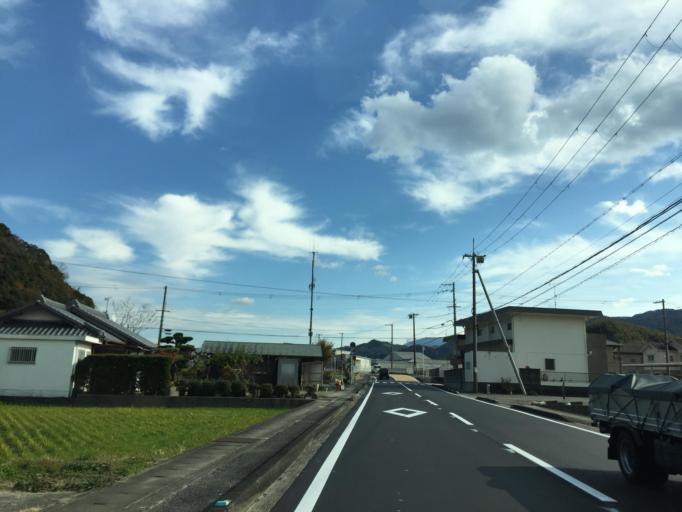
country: JP
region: Wakayama
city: Kainan
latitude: 34.1611
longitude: 135.2623
